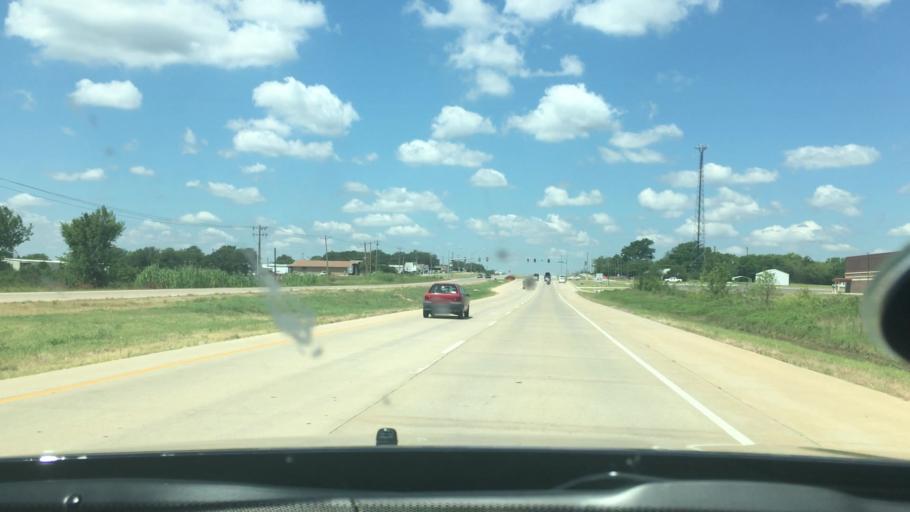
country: US
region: Oklahoma
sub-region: Carter County
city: Lone Grove
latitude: 34.1730
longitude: -97.2441
